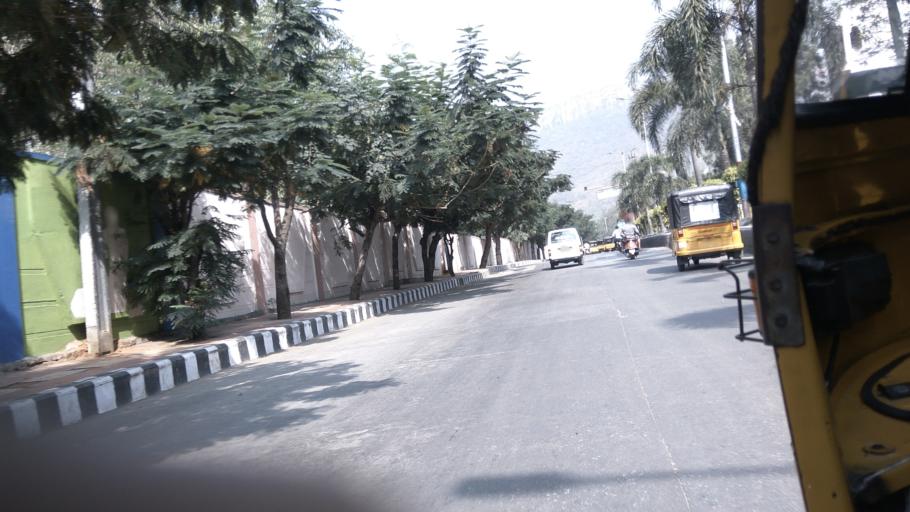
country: IN
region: Andhra Pradesh
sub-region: Chittoor
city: Tirupati
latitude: 13.6413
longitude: 79.4096
